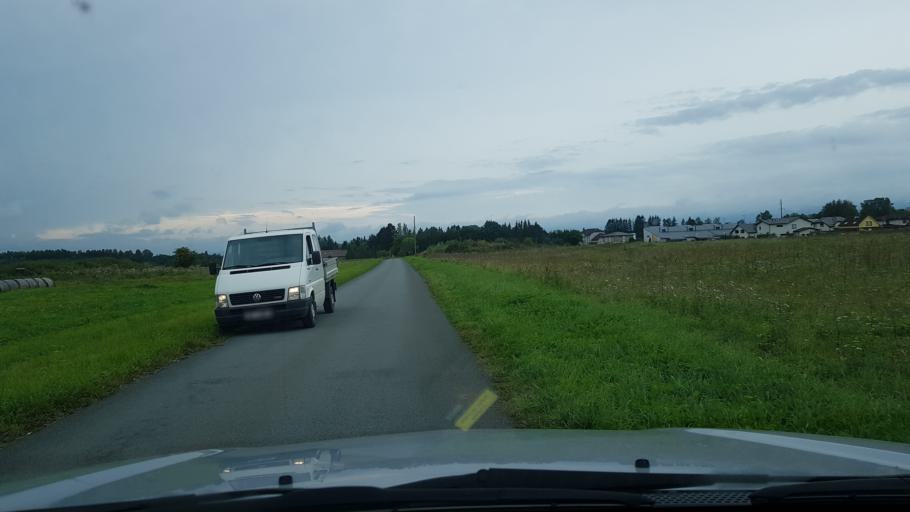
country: EE
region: Harju
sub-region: Joelaehtme vald
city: Loo
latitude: 59.4039
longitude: 24.9529
